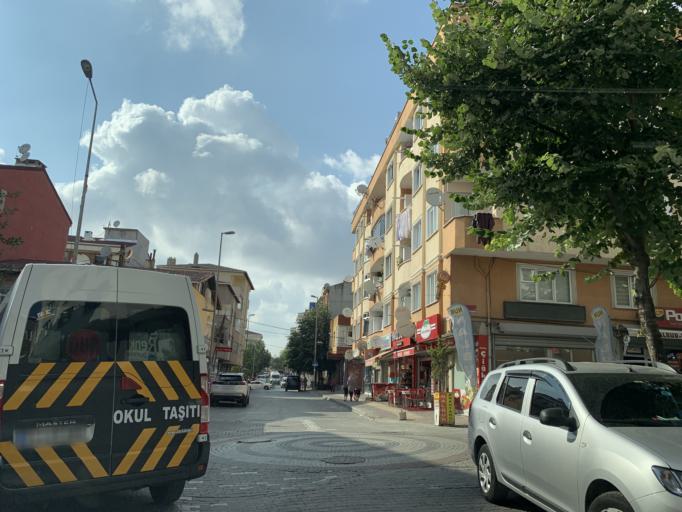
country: TR
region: Istanbul
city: Esenyurt
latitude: 41.0263
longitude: 28.6793
